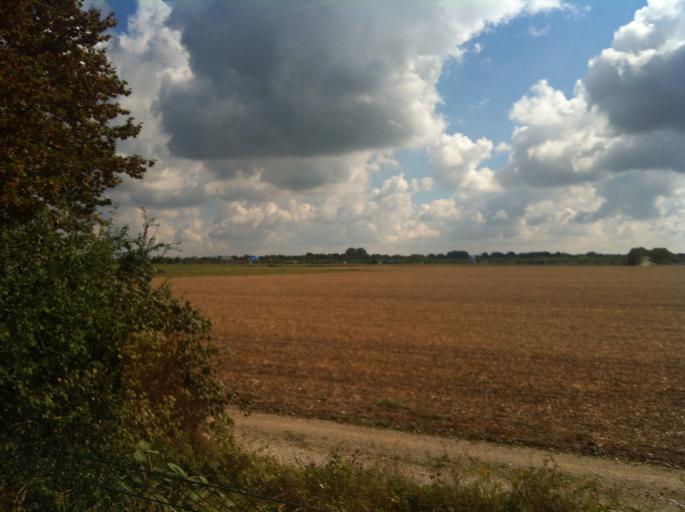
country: DE
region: Bavaria
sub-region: Upper Bavaria
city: Garching bei Munchen
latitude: 48.2353
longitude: 11.6258
